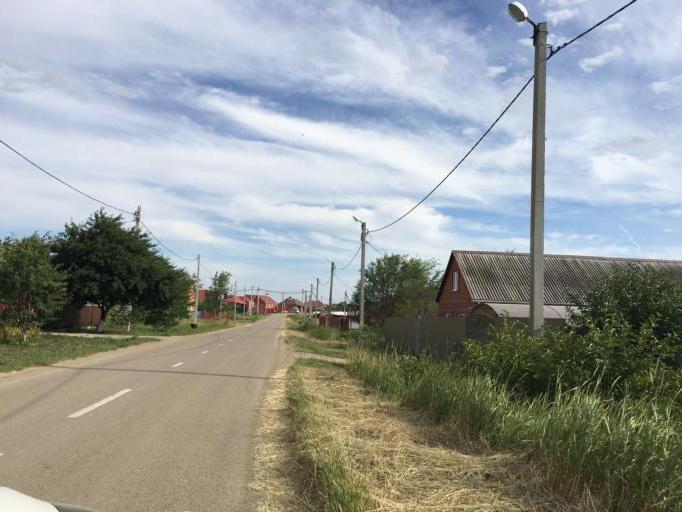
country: RU
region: Krasnodarskiy
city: Kushchevskaya
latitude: 46.5552
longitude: 39.6736
